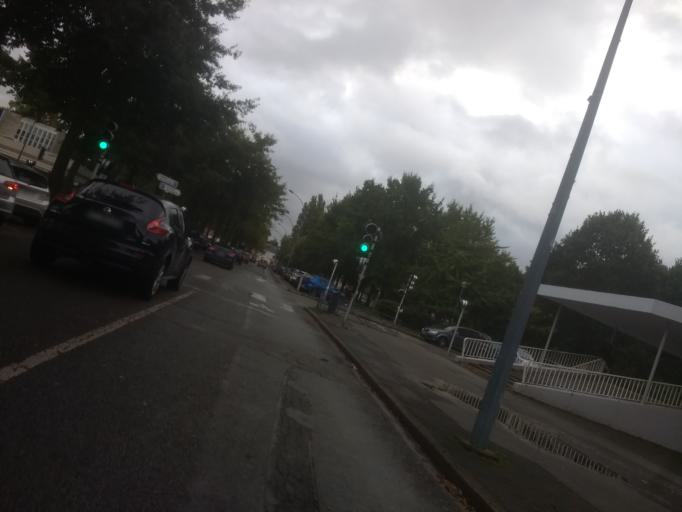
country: FR
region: Nord-Pas-de-Calais
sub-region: Departement du Pas-de-Calais
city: Achicourt
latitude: 50.2875
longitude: 2.7660
